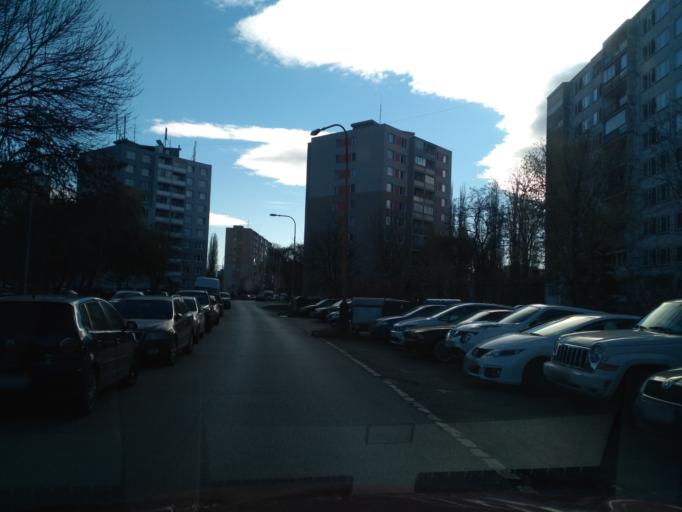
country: SK
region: Kosicky
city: Kosice
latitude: 48.6874
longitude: 21.2894
